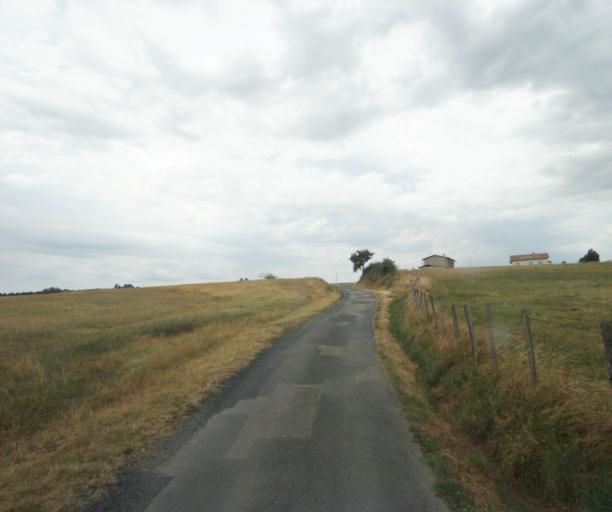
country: FR
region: Rhone-Alpes
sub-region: Departement du Rhone
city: Bully
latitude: 45.8649
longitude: 4.5706
